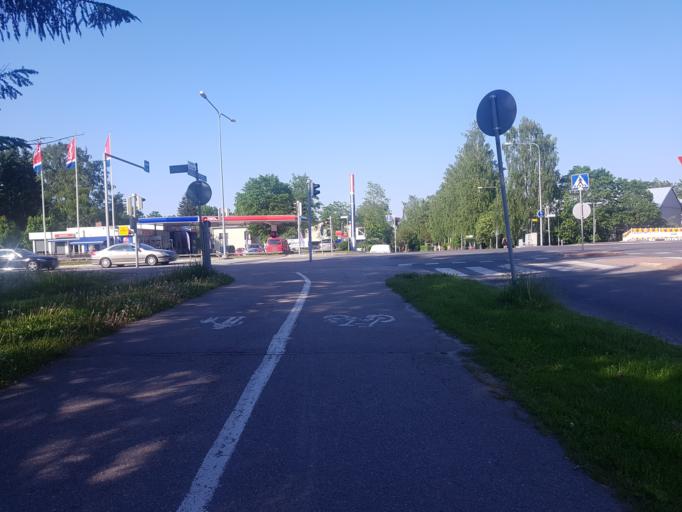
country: FI
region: Uusimaa
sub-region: Helsinki
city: Vantaa
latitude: 60.2567
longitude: 24.9979
